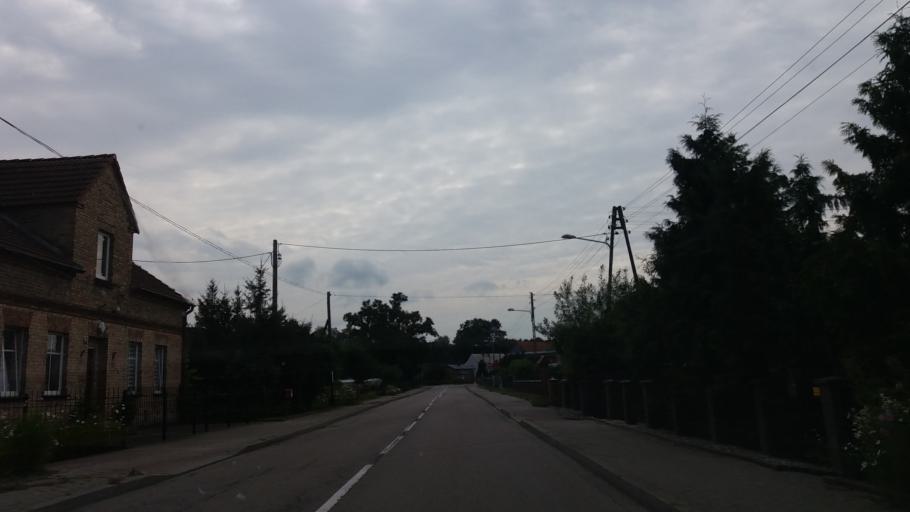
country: PL
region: Lubusz
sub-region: Powiat miedzyrzecki
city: Skwierzyna
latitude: 52.6445
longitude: 15.4529
